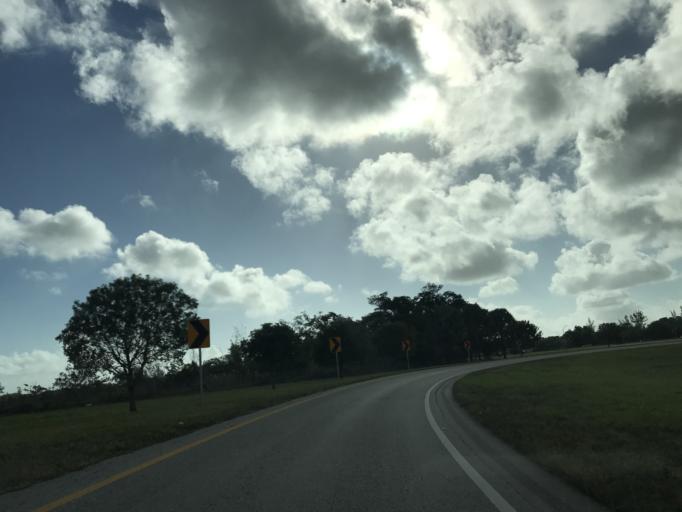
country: US
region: Florida
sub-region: Palm Beach County
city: Boca Pointe
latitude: 26.3085
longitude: -80.1666
